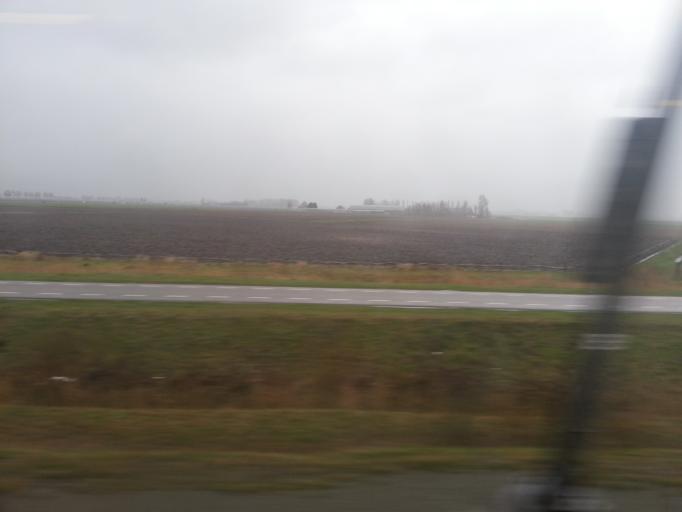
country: NL
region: North Brabant
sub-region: Gemeente Breda
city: Breda
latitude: 51.6420
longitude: 4.6964
